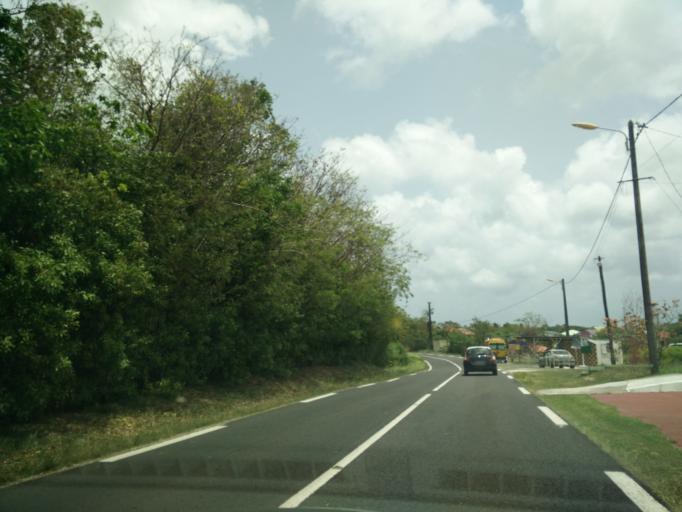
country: GP
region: Guadeloupe
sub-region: Guadeloupe
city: Port-Louis
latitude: 16.4106
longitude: -61.5169
